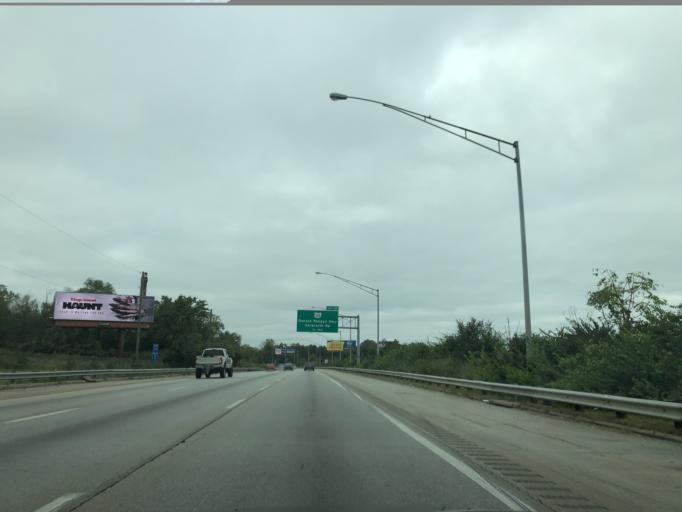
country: US
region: Ohio
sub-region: Hamilton County
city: Lockland
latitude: 39.2213
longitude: -84.4571
